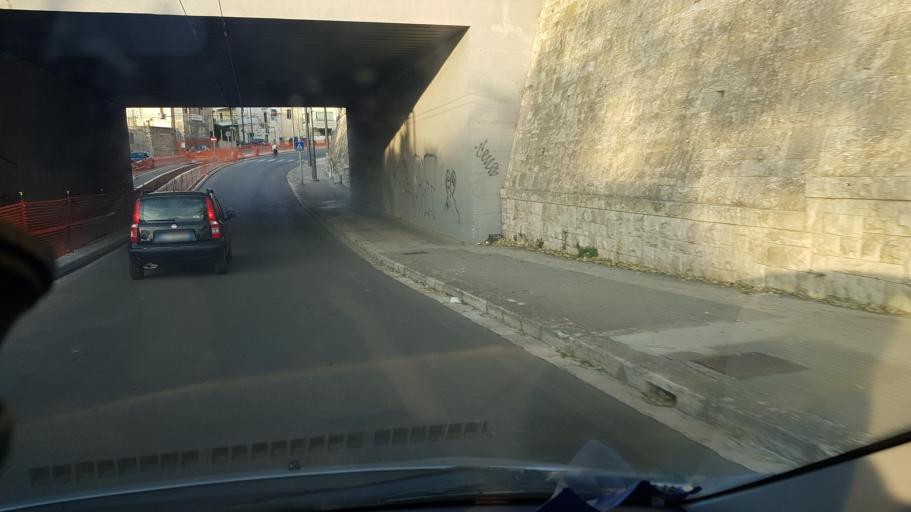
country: IT
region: Apulia
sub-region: Provincia di Lecce
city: Lecce
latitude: 40.3478
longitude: 18.1608
